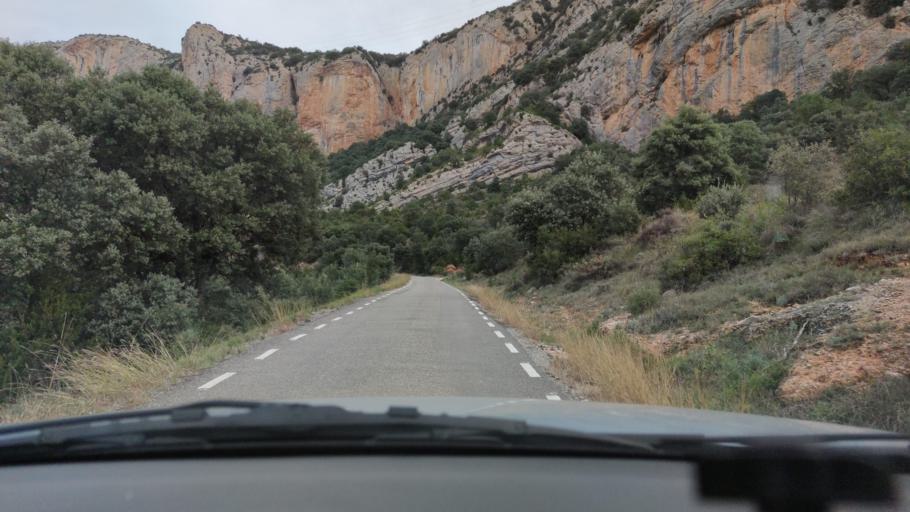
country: ES
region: Catalonia
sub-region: Provincia de Lleida
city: Artesa de Segre
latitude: 42.0218
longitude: 1.0340
